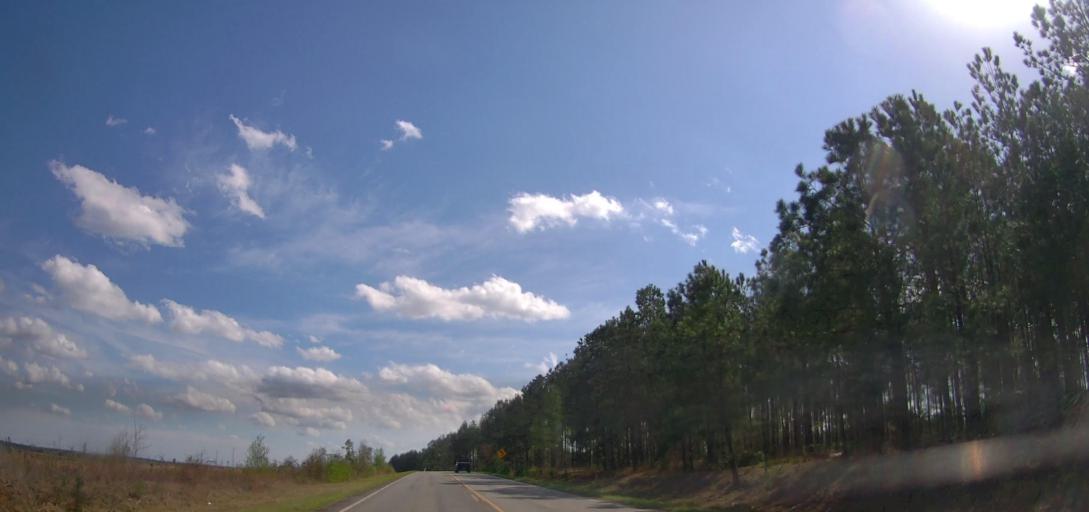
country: US
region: Georgia
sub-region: Wilkinson County
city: Gordon
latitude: 32.9497
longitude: -83.2904
